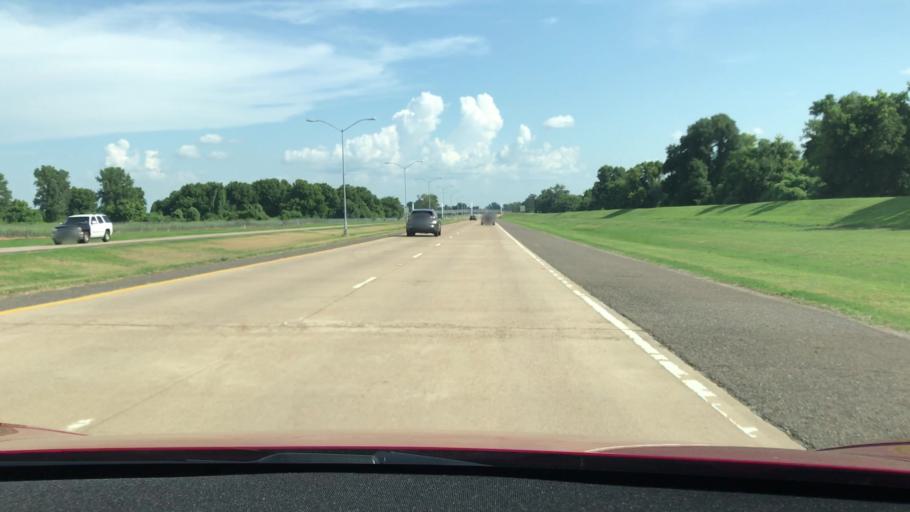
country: US
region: Louisiana
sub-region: Bossier Parish
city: Bossier City
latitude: 32.4754
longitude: -93.6791
